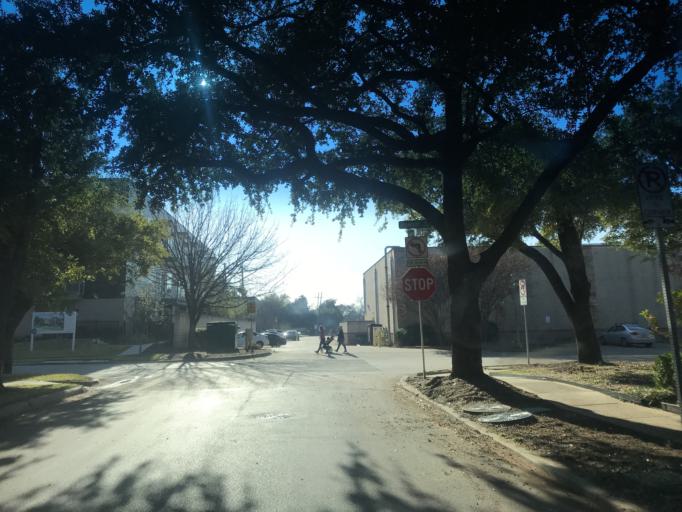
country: US
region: Texas
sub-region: Dallas County
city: Highland Park
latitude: 32.8208
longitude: -96.8135
